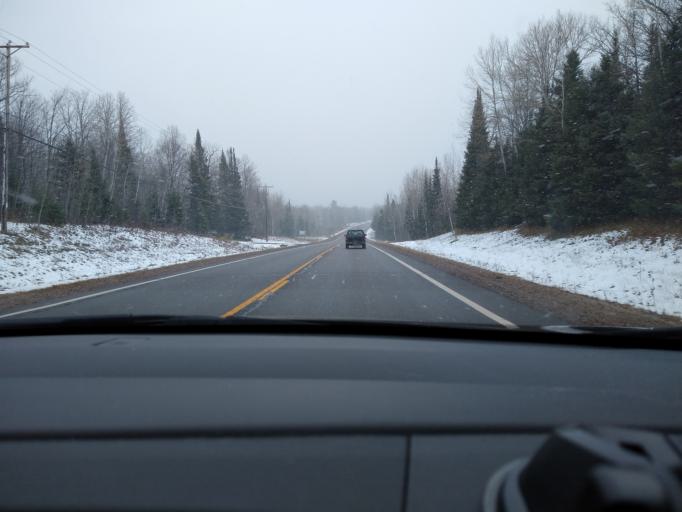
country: US
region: Wisconsin
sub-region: Florence County
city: Florence
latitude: 46.0628
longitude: -88.0712
